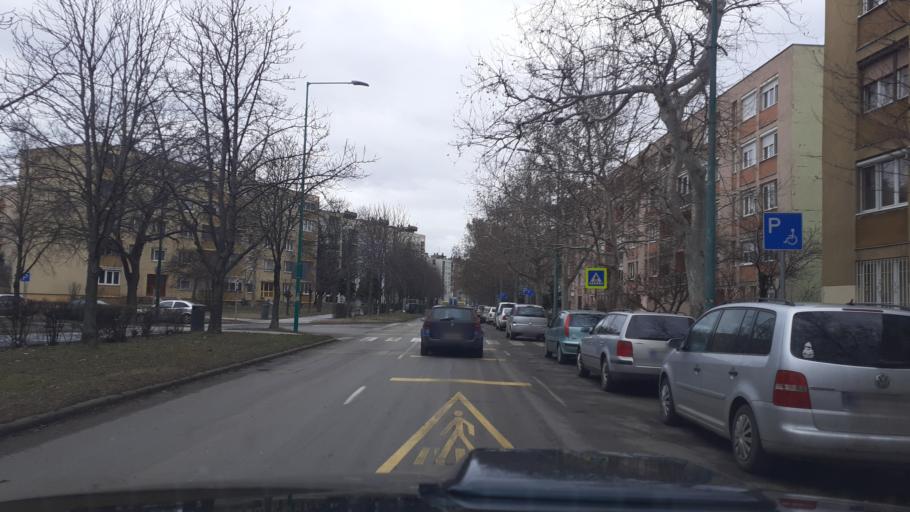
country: HU
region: Fejer
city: dunaujvaros
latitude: 46.9709
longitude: 18.9372
